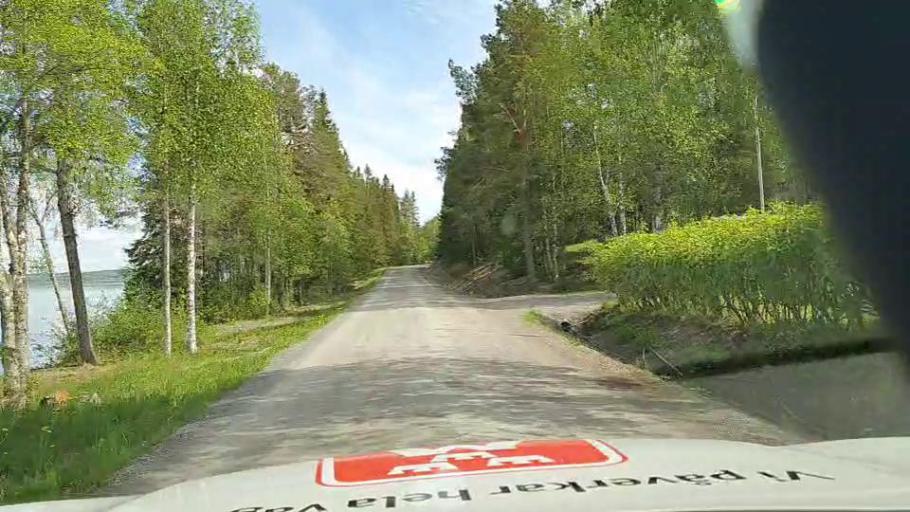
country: SE
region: Jaemtland
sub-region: OEstersunds Kommun
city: Brunflo
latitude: 63.0093
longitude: 14.7848
